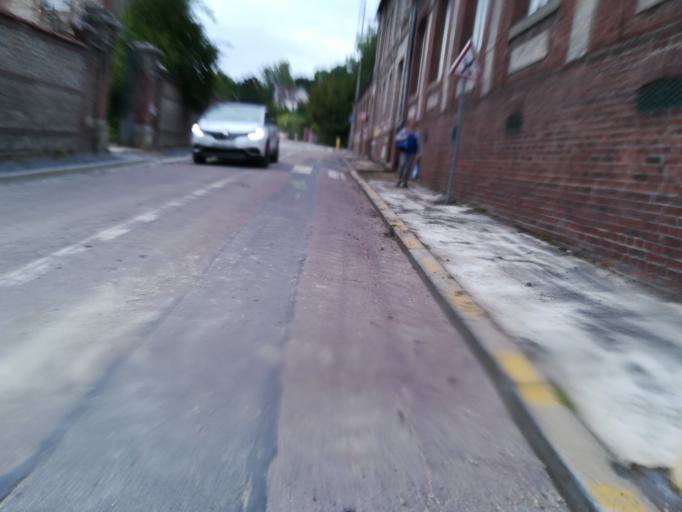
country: FR
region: Haute-Normandie
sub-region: Departement de la Seine-Maritime
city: Mont-Saint-Aignan
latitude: 49.4594
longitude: 1.0891
